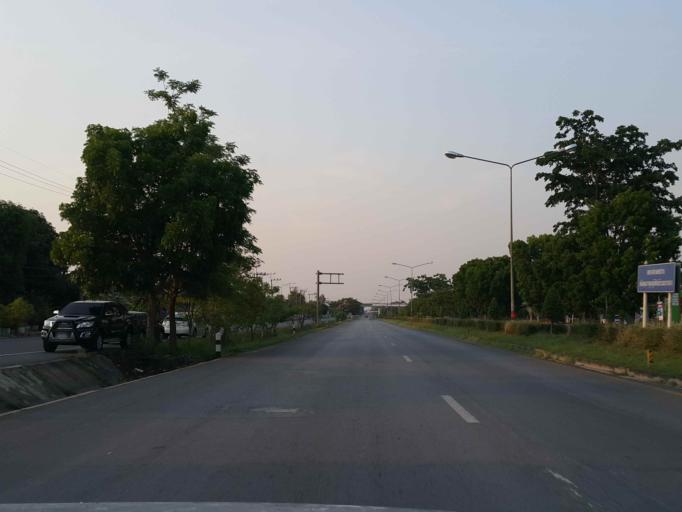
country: TH
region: Lampang
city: Sop Prap
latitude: 17.8766
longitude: 99.3371
